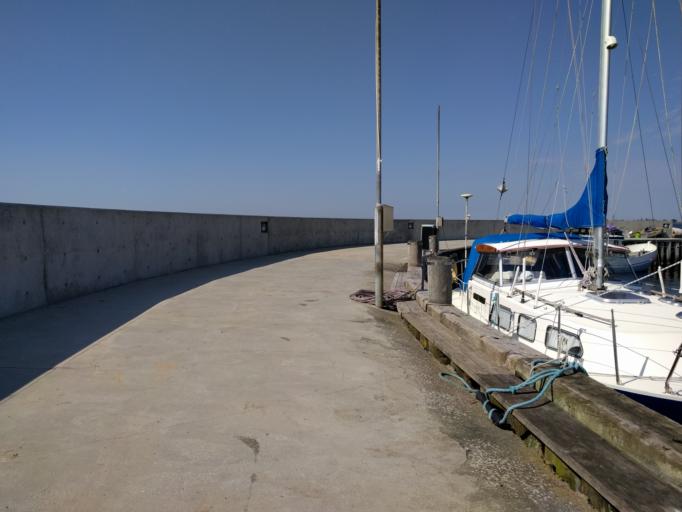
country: DK
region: South Denmark
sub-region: Kerteminde Kommune
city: Munkebo
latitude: 55.4861
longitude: 10.5973
